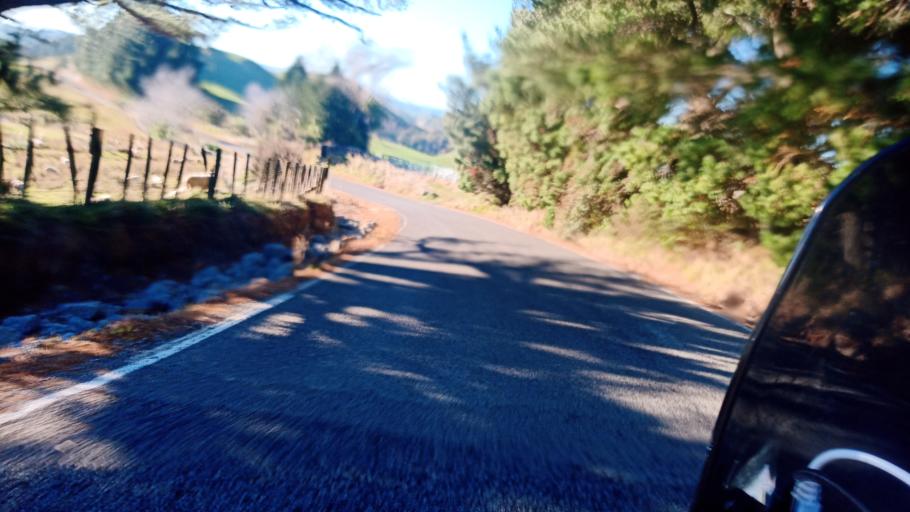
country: NZ
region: Hawke's Bay
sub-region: Wairoa District
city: Wairoa
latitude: -38.8324
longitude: 177.2755
